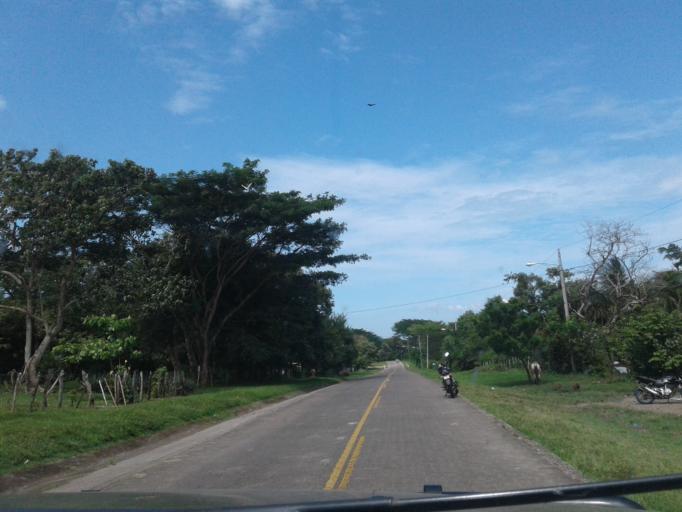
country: NI
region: Rivas
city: Cardenas
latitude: 11.1785
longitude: -85.4888
